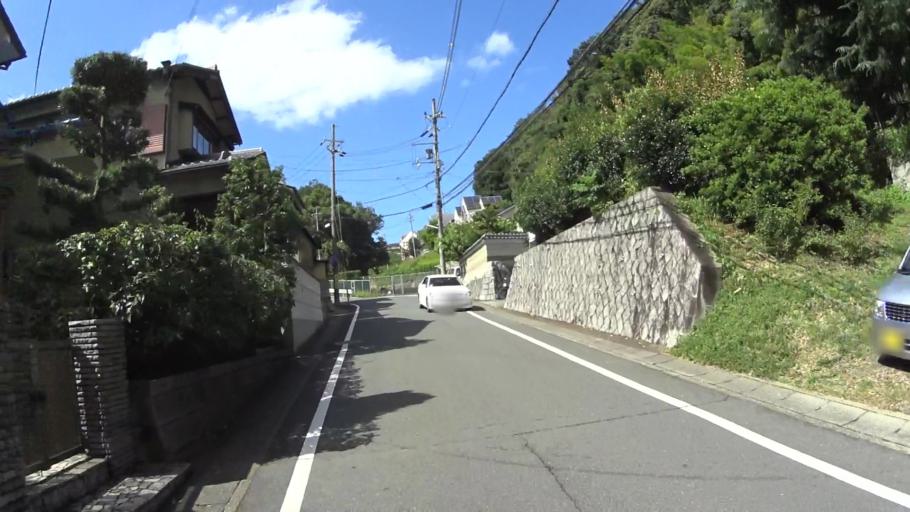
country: JP
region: Kyoto
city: Uji
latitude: 34.9382
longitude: 135.7893
